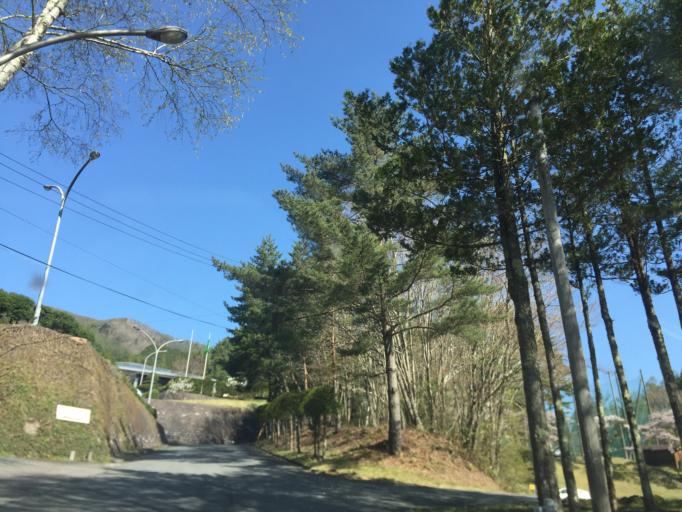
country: JP
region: Nagano
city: Iida
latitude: 35.4101
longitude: 137.6719
